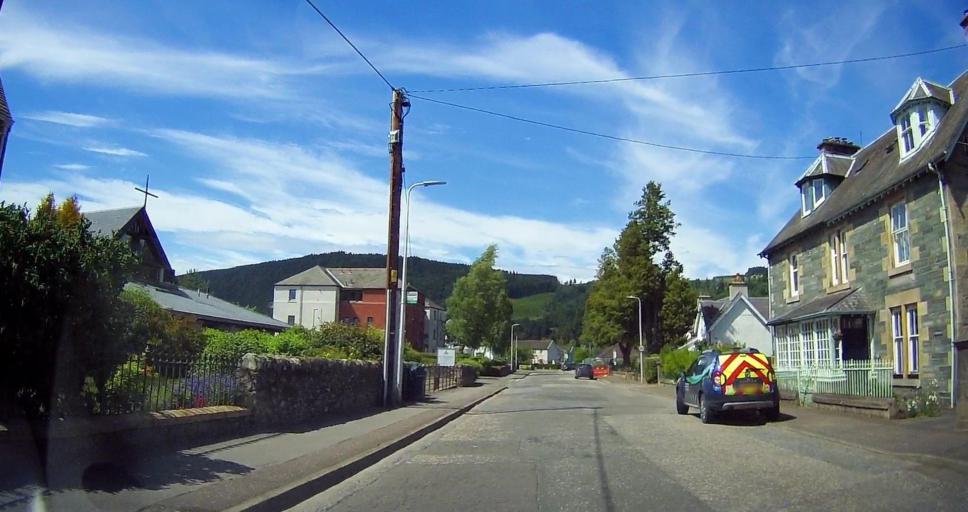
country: GB
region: Scotland
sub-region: Perth and Kinross
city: Aberfeldy
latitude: 56.6220
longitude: -3.8624
